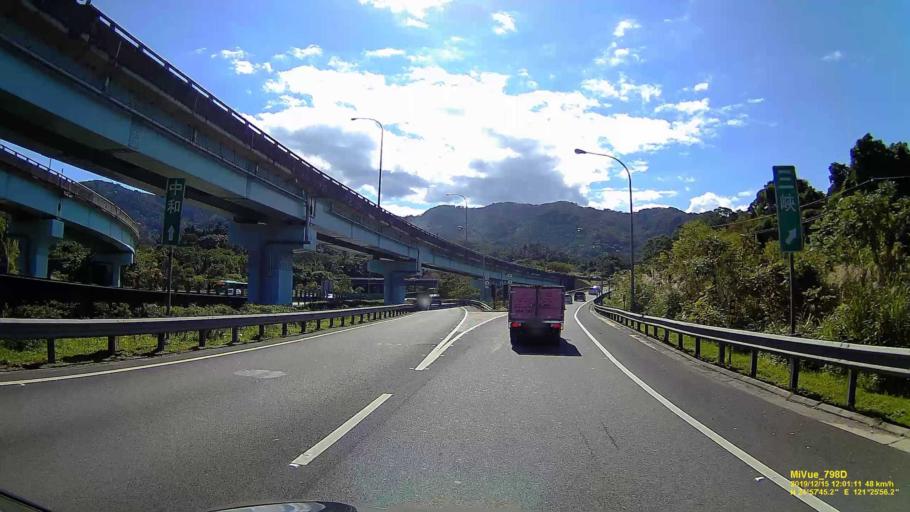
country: TW
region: Taipei
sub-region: Taipei
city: Banqiao
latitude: 24.9624
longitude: 121.4322
